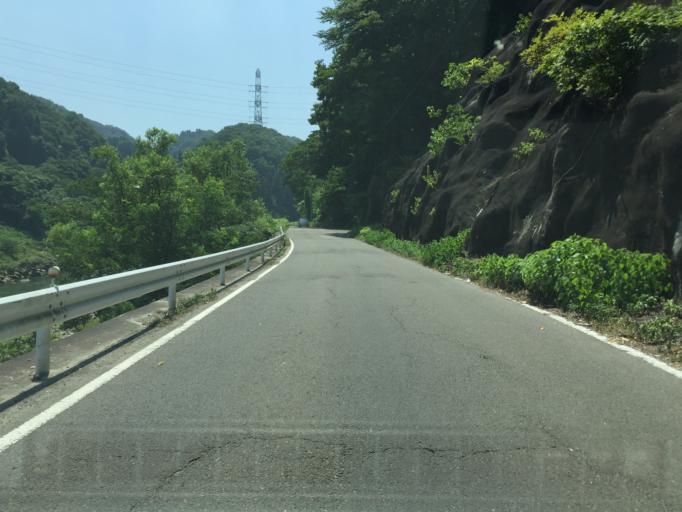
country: JP
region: Miyagi
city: Marumori
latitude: 37.9164
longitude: 140.6870
